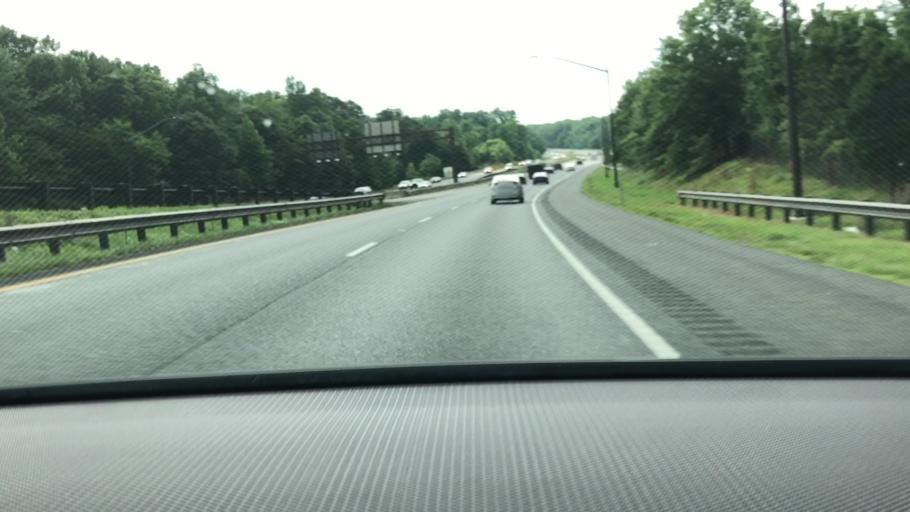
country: US
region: Maryland
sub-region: Anne Arundel County
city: Riva
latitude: 38.9872
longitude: -76.5774
